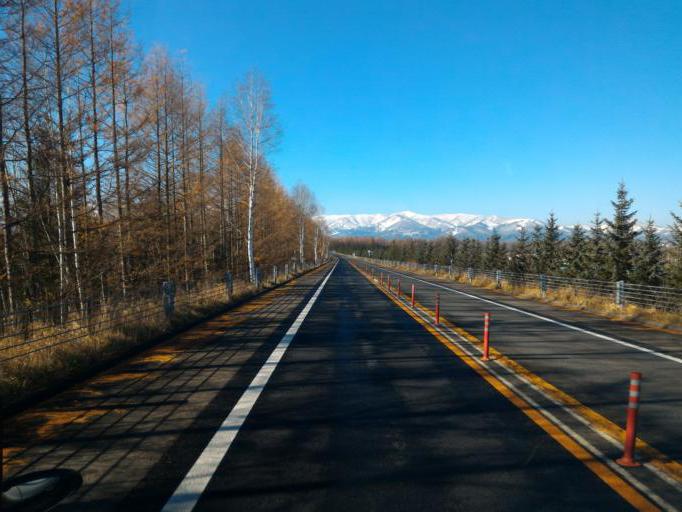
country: JP
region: Hokkaido
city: Otofuke
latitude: 42.9788
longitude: 142.9465
